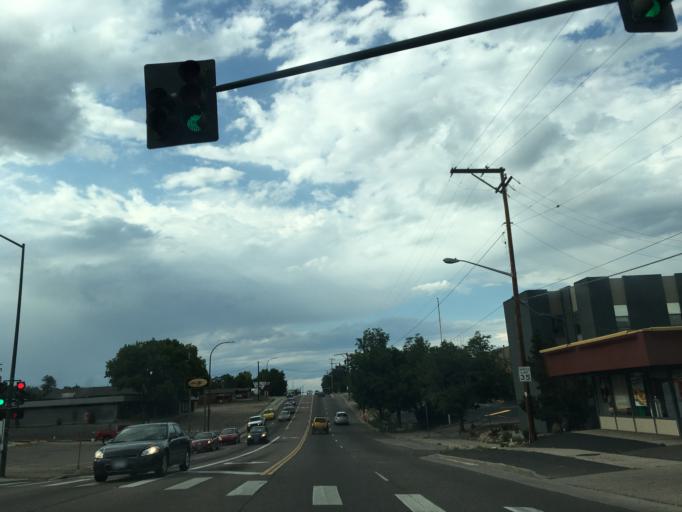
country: US
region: Colorado
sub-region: Jefferson County
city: Lakewood
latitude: 39.7182
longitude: -105.0533
